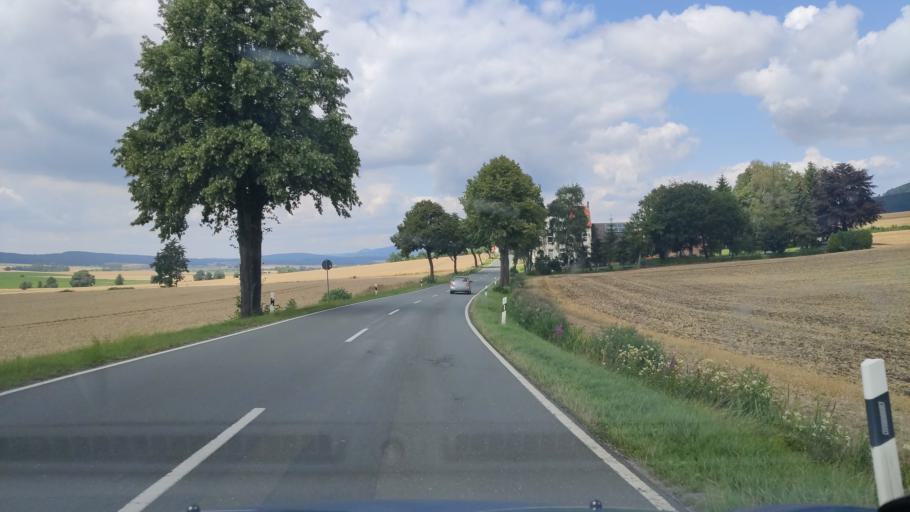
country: DE
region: Lower Saxony
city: Heyen
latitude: 52.0659
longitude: 9.5211
